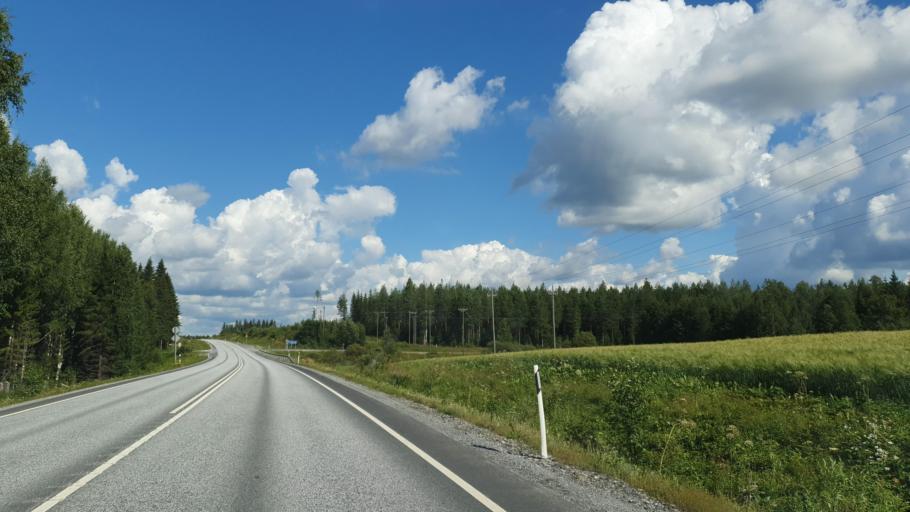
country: FI
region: Northern Savo
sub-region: Ylae-Savo
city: Sonkajaervi
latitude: 63.8475
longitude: 27.4390
